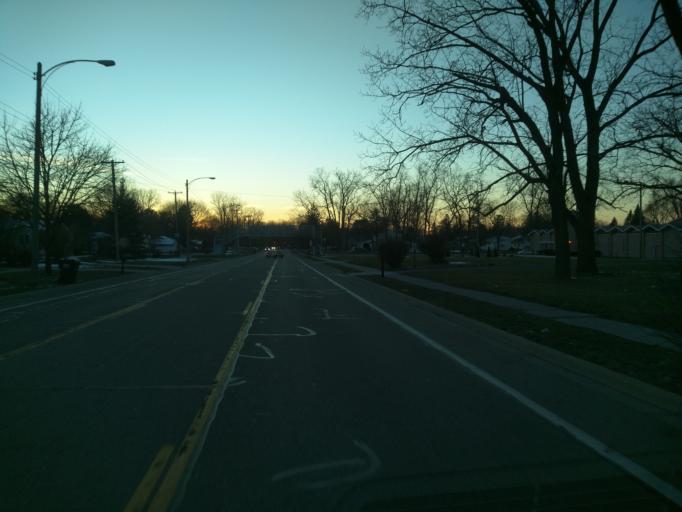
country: US
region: Michigan
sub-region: Eaton County
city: Waverly
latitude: 42.6976
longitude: -84.5975
